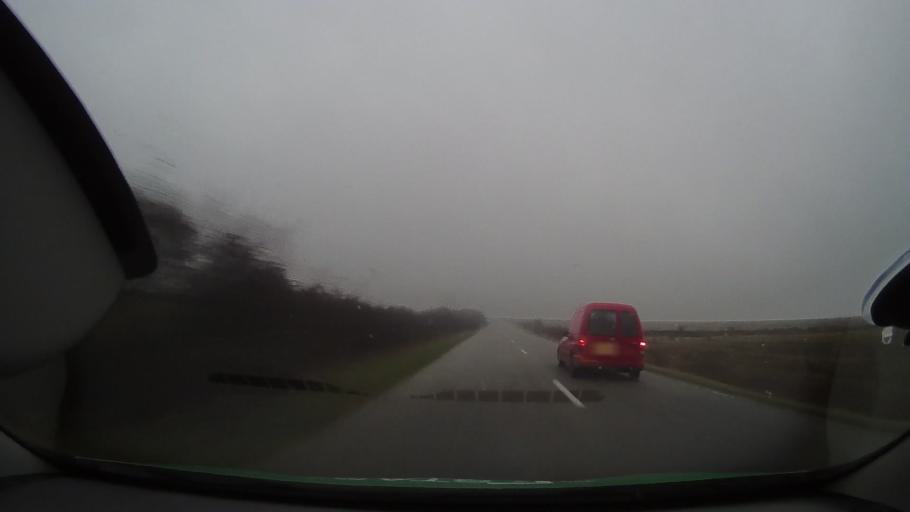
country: RO
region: Arad
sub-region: Comuna Craiova
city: Craiova
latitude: 46.6130
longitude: 21.9566
